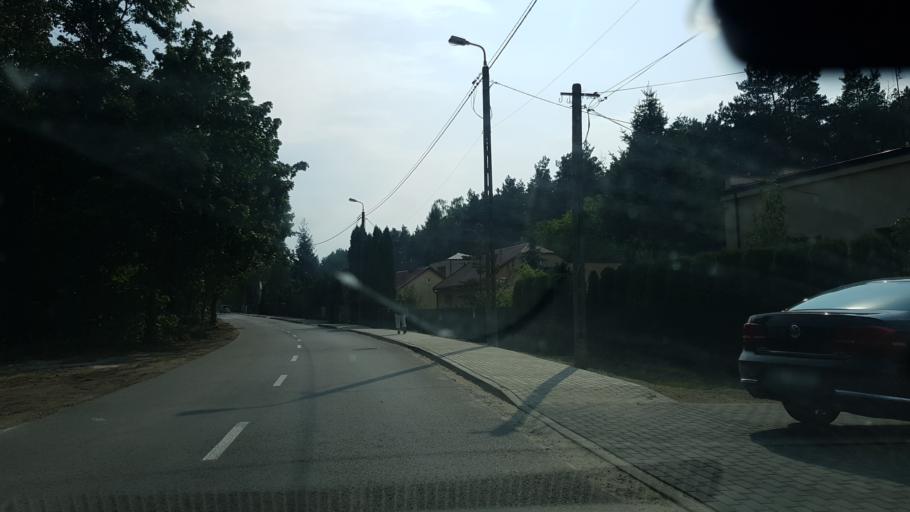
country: PL
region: Masovian Voivodeship
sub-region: Powiat piaseczynski
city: Konstancin-Jeziorna
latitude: 52.0644
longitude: 21.0987
